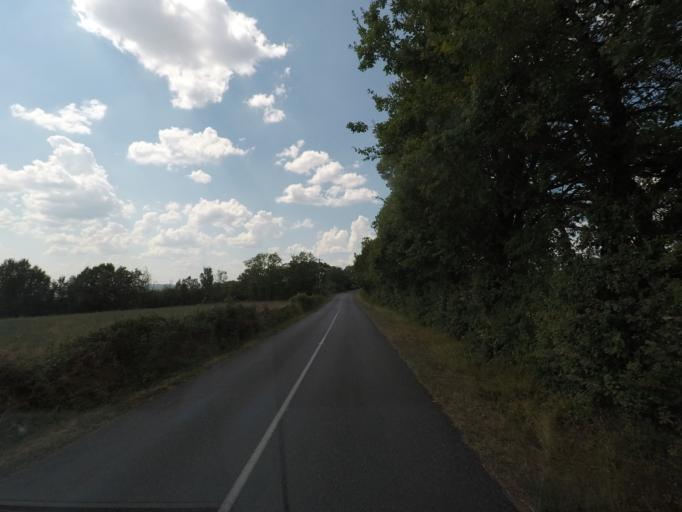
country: FR
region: Midi-Pyrenees
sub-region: Departement du Lot
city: Le Vigan
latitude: 44.6377
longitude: 1.5895
